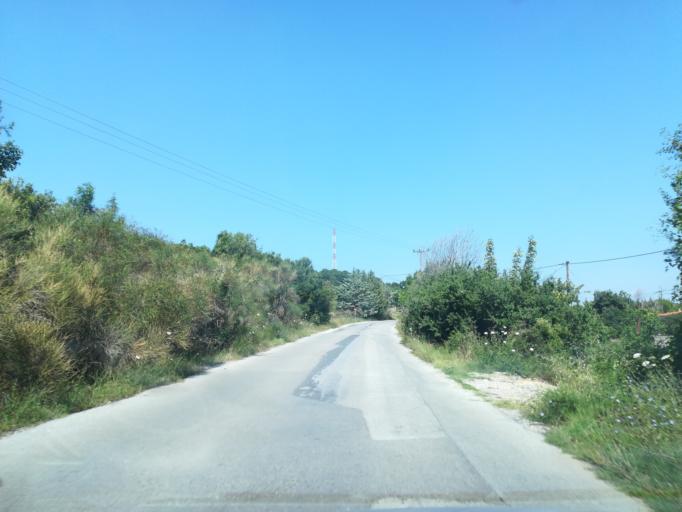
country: GR
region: Central Macedonia
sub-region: Nomos Thessalonikis
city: Asvestochori
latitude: 40.6333
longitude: 23.0249
